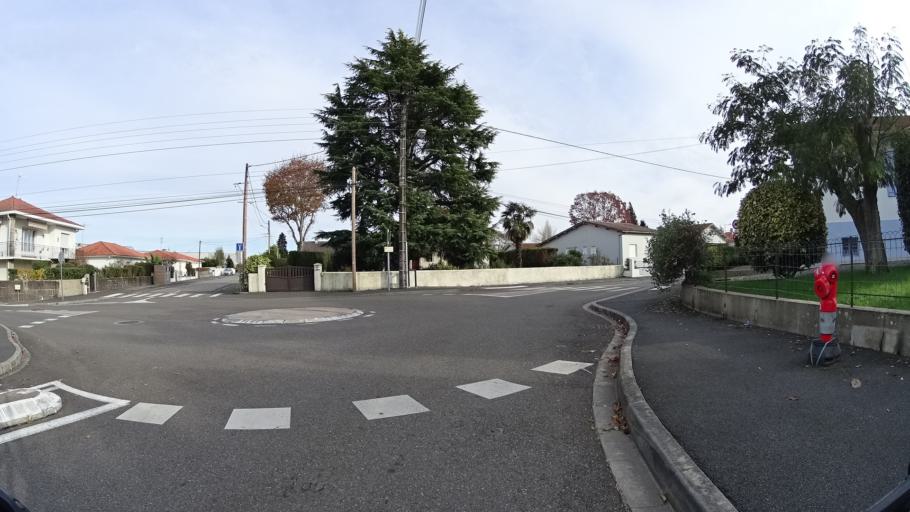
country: FR
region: Aquitaine
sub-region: Departement des Landes
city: Saint-Paul-les-Dax
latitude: 43.7301
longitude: -1.0452
